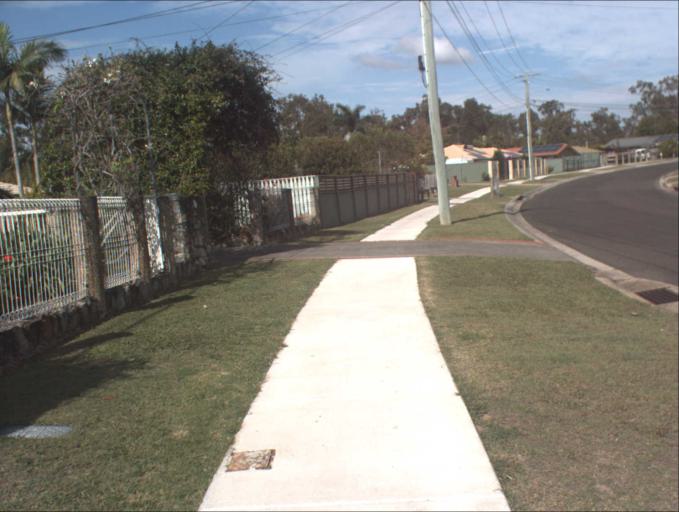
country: AU
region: Queensland
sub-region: Logan
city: Park Ridge South
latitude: -27.6735
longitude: 153.0417
